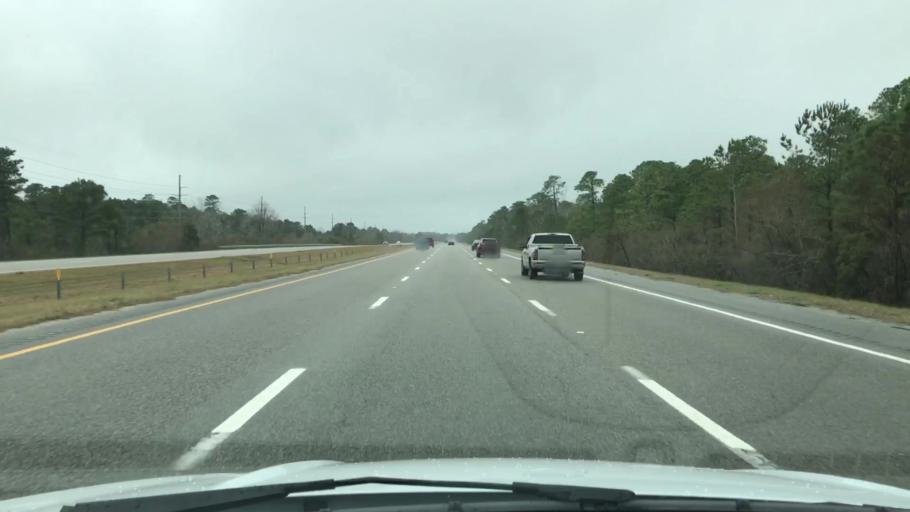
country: US
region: South Carolina
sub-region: Horry County
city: Forestbrook
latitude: 33.7471
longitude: -78.9131
